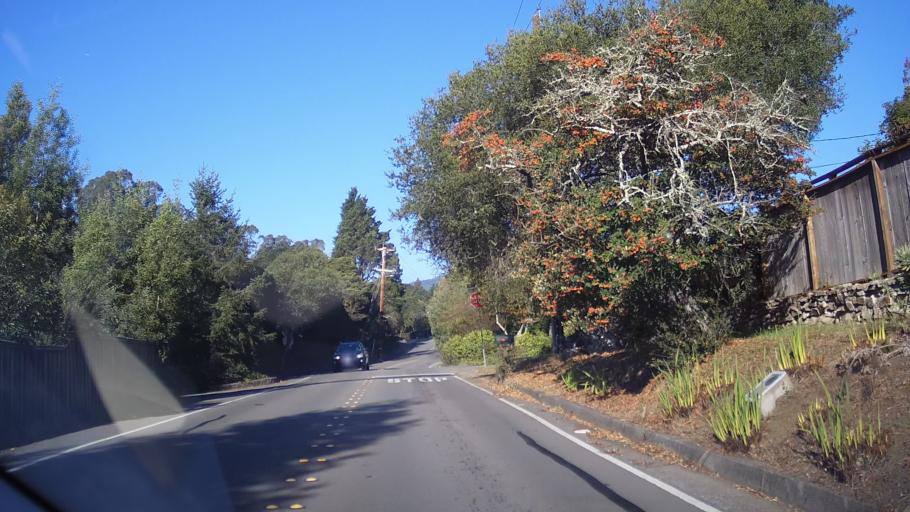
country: US
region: California
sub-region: Marin County
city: Mill Valley
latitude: 37.9003
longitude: -122.5482
